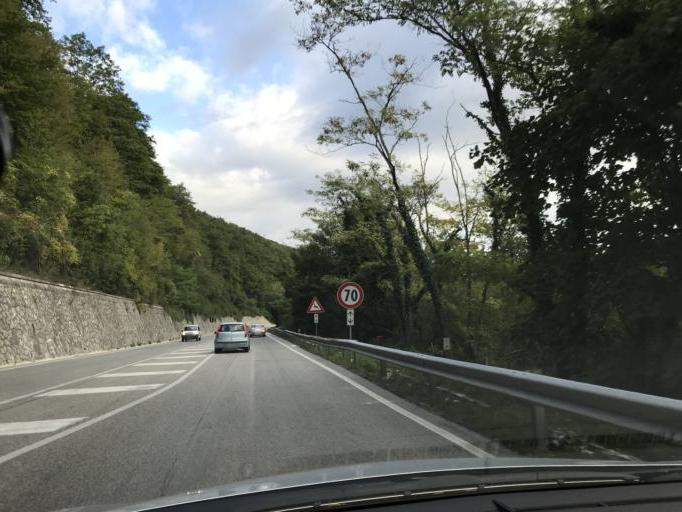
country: IT
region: Umbria
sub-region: Provincia di Perugia
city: Spoleto
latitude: 42.6900
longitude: 12.7222
